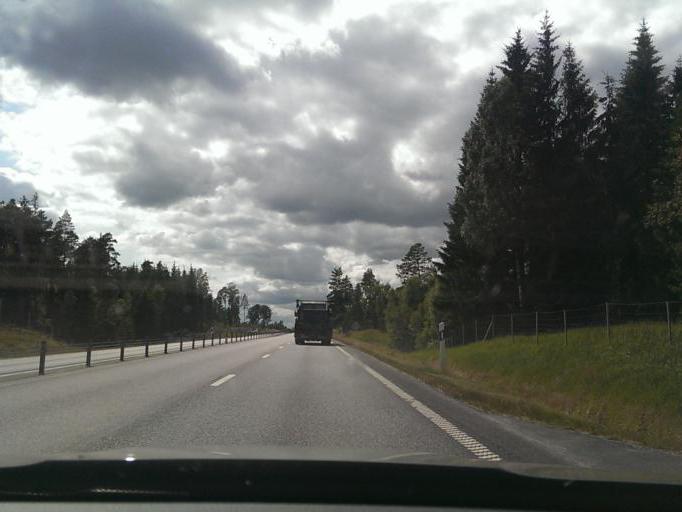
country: SE
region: Joenkoeping
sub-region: Varnamo Kommun
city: Varnamo
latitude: 57.1839
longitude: 13.9497
